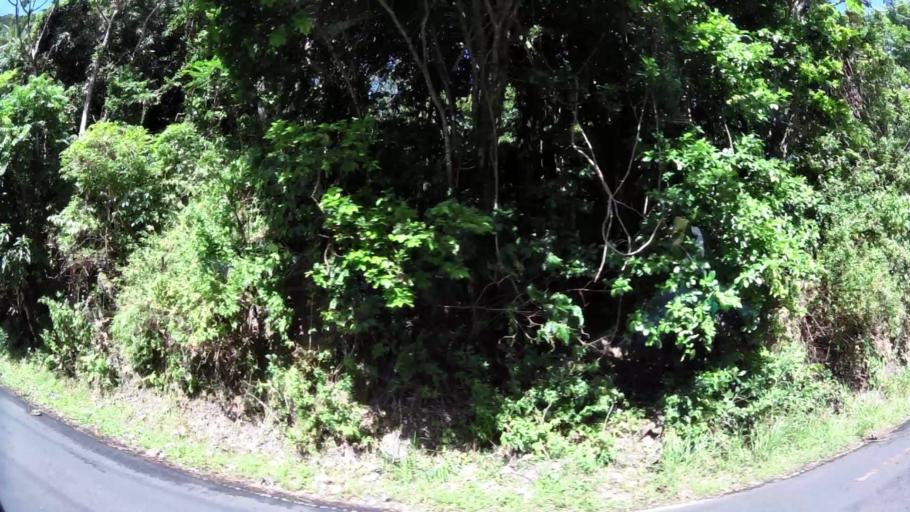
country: LC
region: Soufriere
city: Soufriere
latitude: 13.8285
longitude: -61.0489
